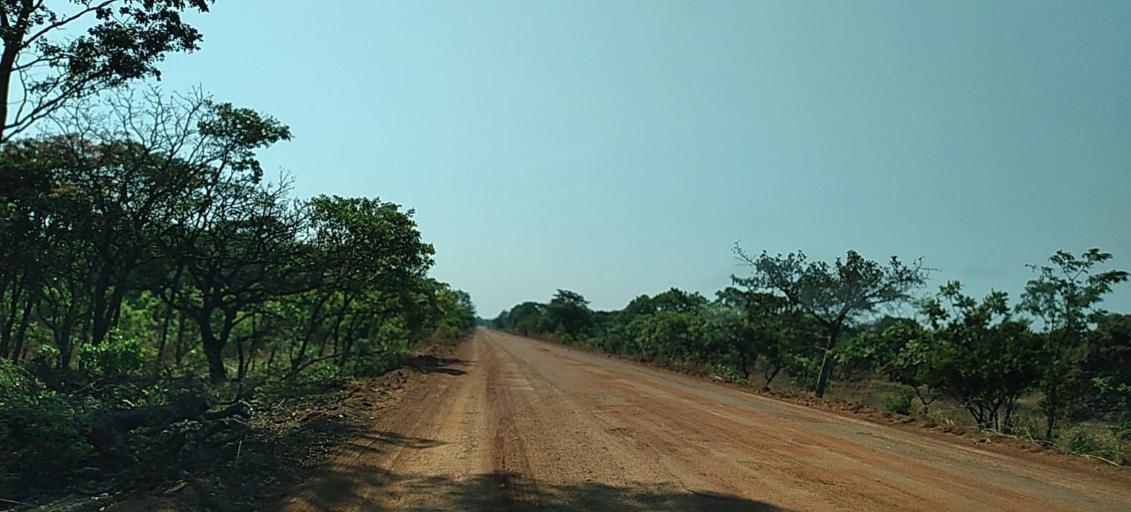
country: ZM
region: North-Western
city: Mwinilunga
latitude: -11.9149
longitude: 25.3059
